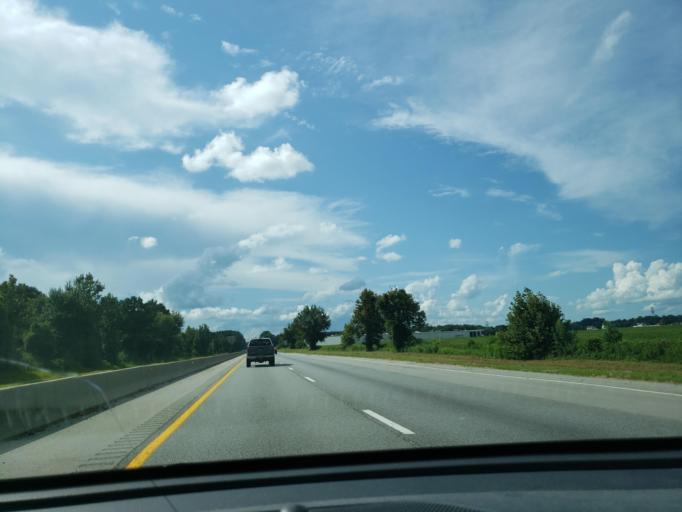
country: US
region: Virginia
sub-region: City of Franklin
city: Franklin
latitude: 36.6527
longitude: -76.9216
